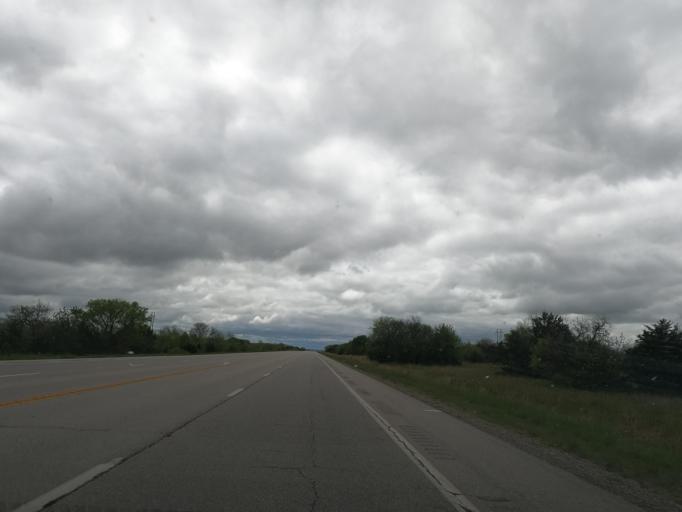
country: US
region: Kansas
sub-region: Wilson County
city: Neodesha
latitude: 37.4814
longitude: -95.7275
